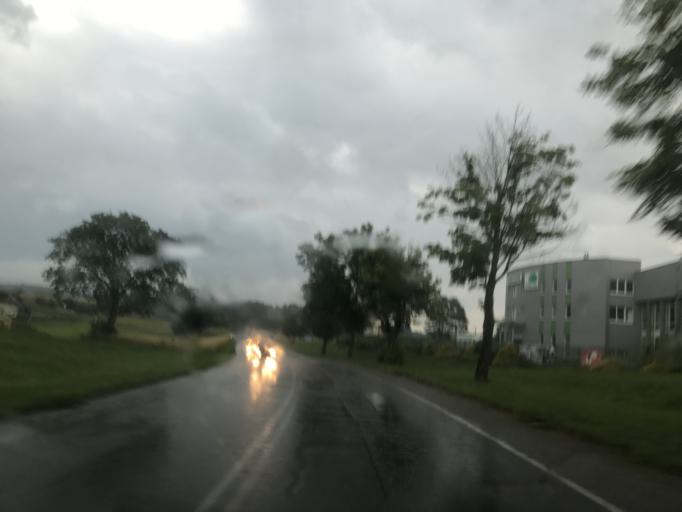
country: PL
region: Pomeranian Voivodeship
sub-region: Powiat chojnicki
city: Chojnice
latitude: 53.7020
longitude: 17.6095
